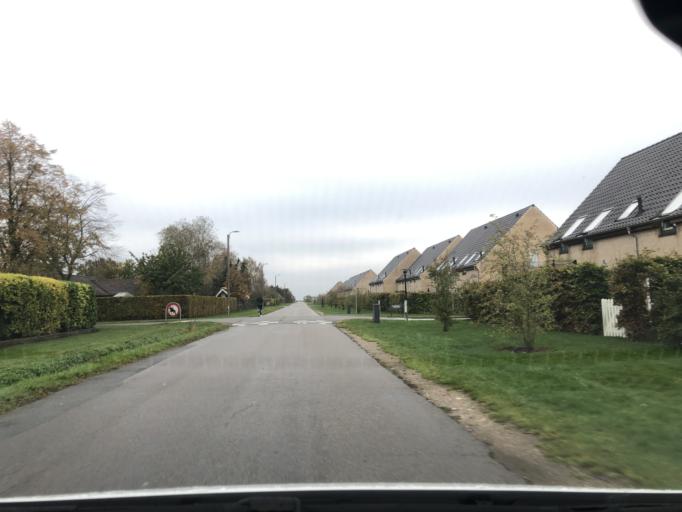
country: DK
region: Capital Region
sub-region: Dragor Kommune
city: Dragor
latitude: 55.5828
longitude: 12.6394
